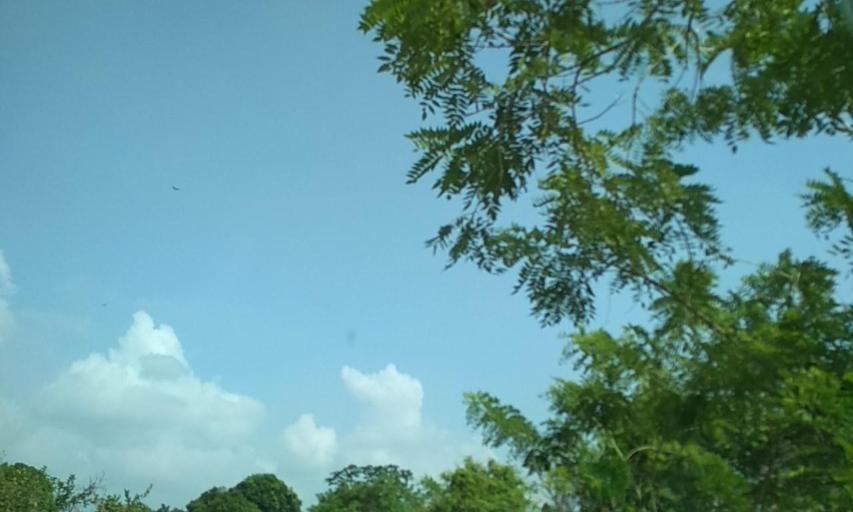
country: MX
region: Veracruz
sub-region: Martinez de la Torre
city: El Progreso
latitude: 20.1470
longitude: -97.0599
